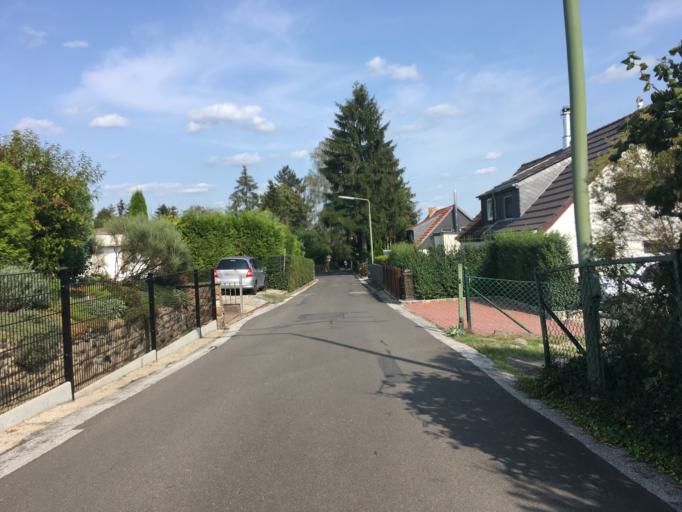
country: DE
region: Berlin
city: Lubars
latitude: 52.6205
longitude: 13.3390
